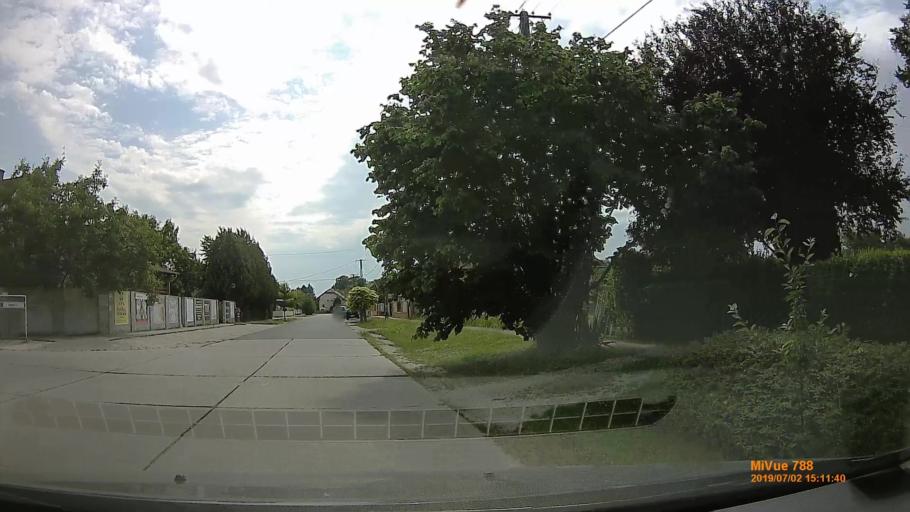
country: HU
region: Gyor-Moson-Sopron
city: Mosonmagyarovar
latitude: 47.8800
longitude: 17.2853
